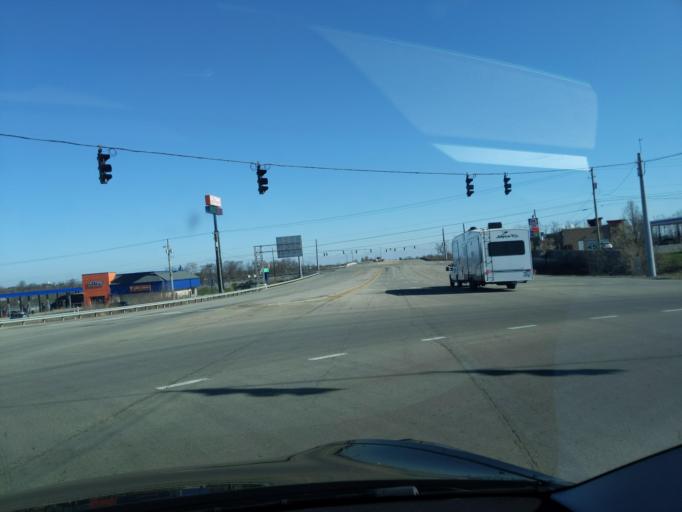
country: US
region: Kentucky
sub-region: Clark County
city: Winchester
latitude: 38.0118
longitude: -84.2082
